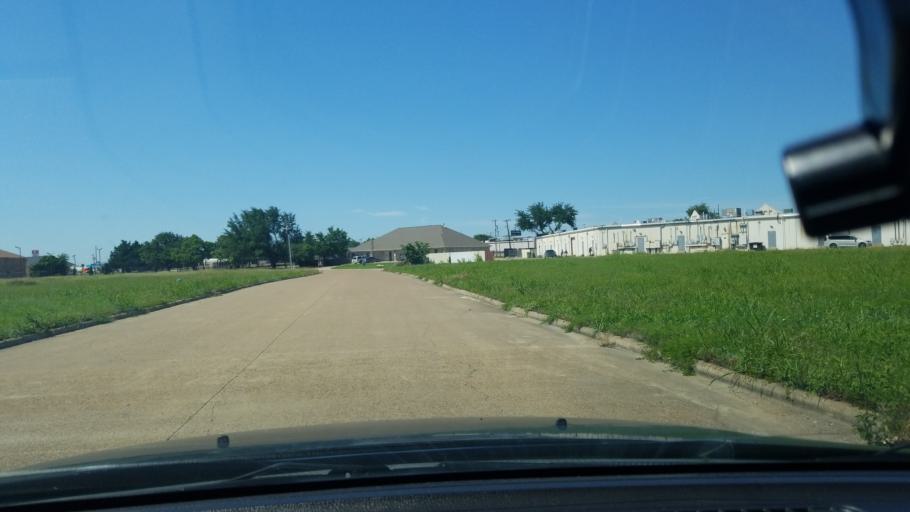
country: US
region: Texas
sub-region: Dallas County
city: Mesquite
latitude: 32.7761
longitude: -96.6219
